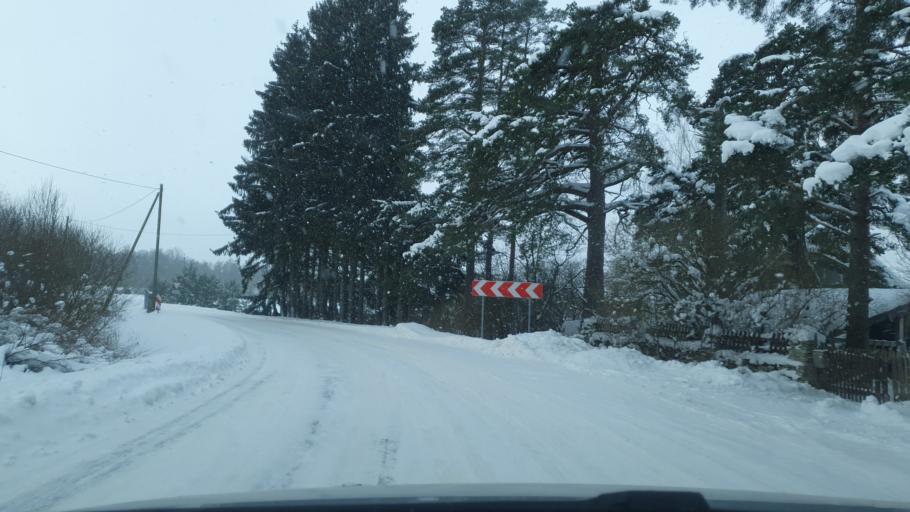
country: EE
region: Harju
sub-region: Kuusalu vald
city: Kuusalu
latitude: 59.4832
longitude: 25.3430
